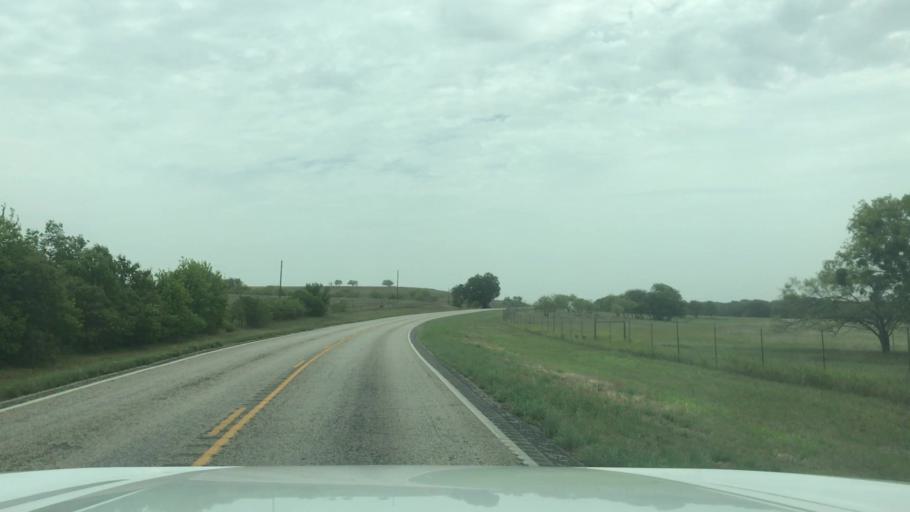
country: US
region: Texas
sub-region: Erath County
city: Dublin
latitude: 32.0574
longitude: -98.1882
